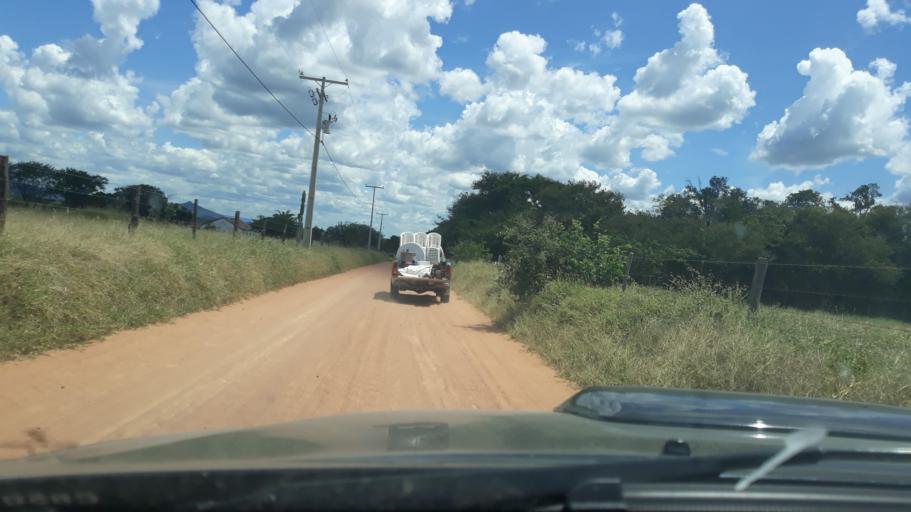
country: BR
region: Bahia
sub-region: Riacho De Santana
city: Riacho de Santana
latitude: -13.9033
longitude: -42.8965
